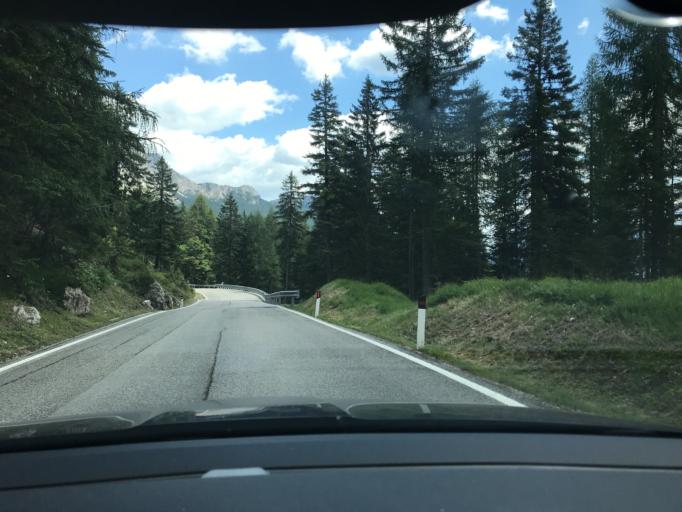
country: IT
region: Veneto
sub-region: Provincia di Belluno
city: Cortina d'Ampezzo
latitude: 46.5569
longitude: 12.2313
